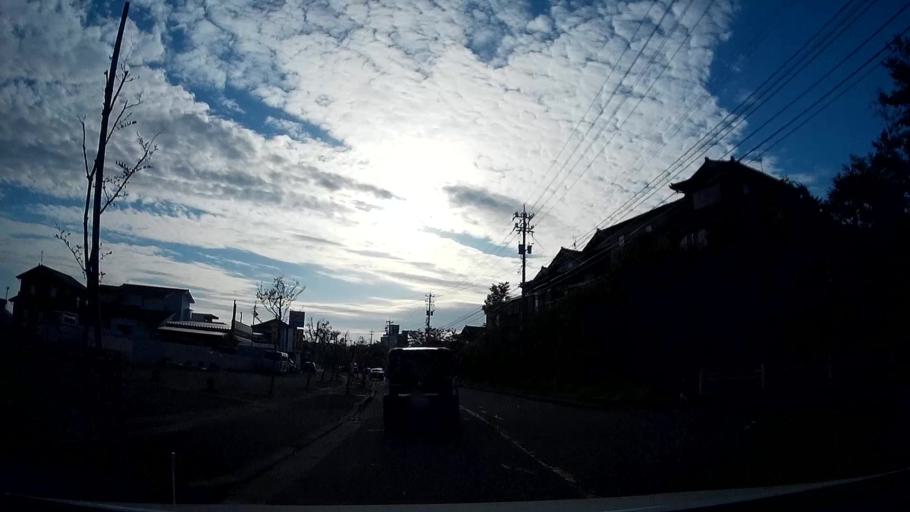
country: JP
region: Ishikawa
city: Nanao
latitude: 37.0840
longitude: 136.9316
